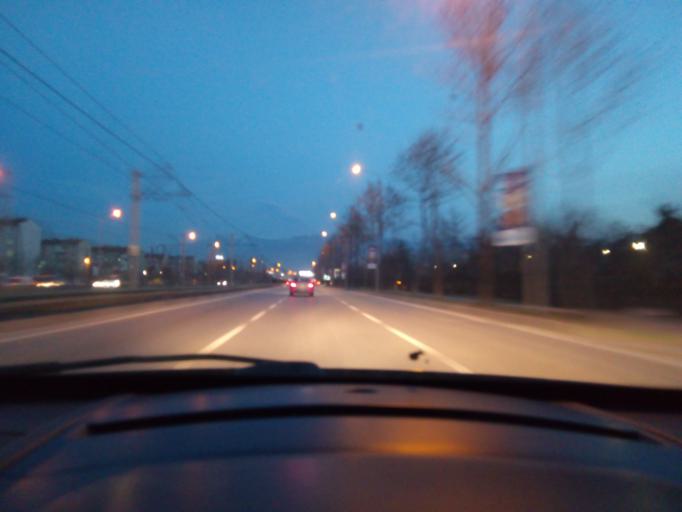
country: TR
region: Bursa
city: Niluefer
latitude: 40.2430
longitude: 28.9674
